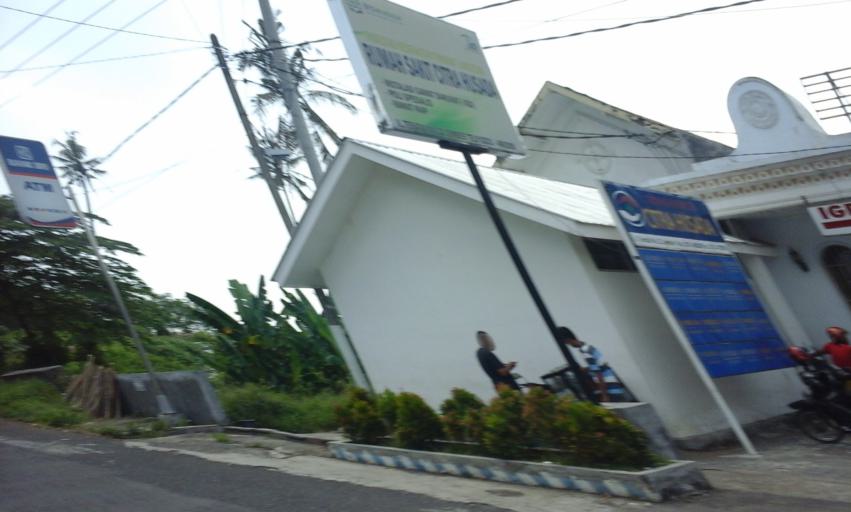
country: ID
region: East Java
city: Kebonwaru Satu
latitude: -8.1668
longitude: 113.6808
